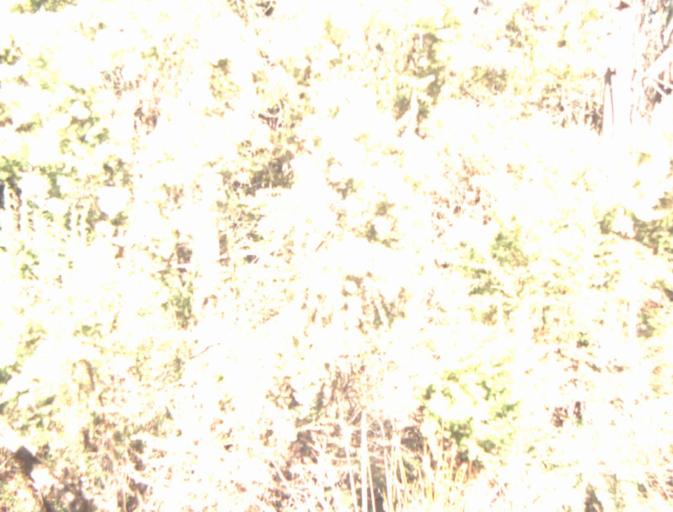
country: AU
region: Tasmania
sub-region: Dorset
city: Scottsdale
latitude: -41.3036
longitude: 147.3589
